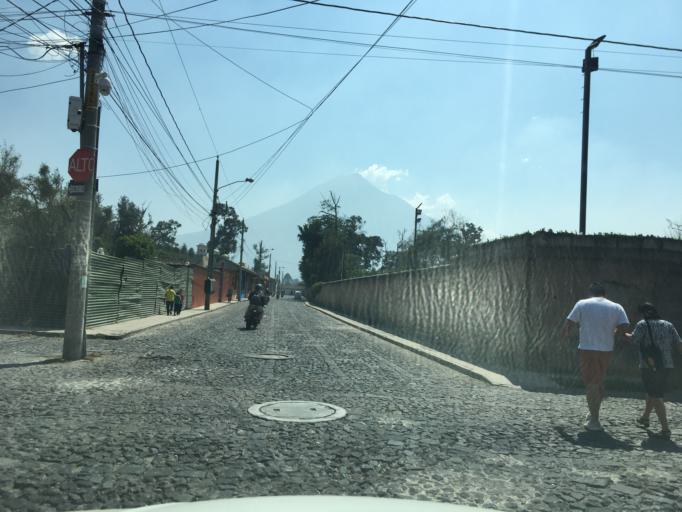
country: GT
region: Sacatepequez
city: Antigua Guatemala
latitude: 14.5629
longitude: -90.7394
